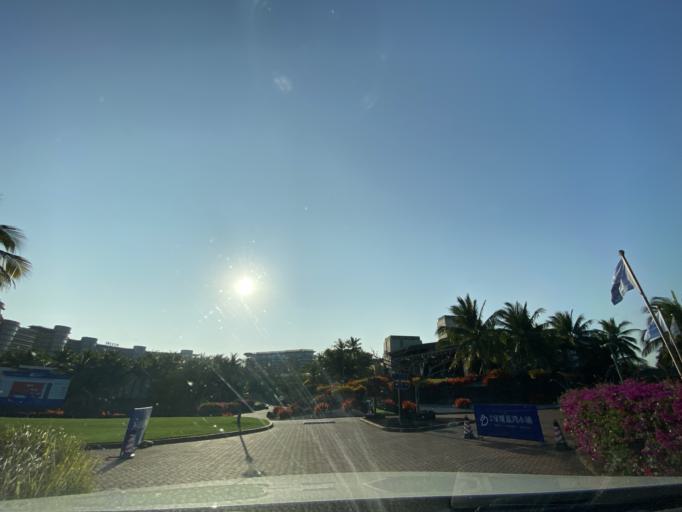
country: CN
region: Hainan
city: Xincun
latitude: 18.4186
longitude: 109.9526
